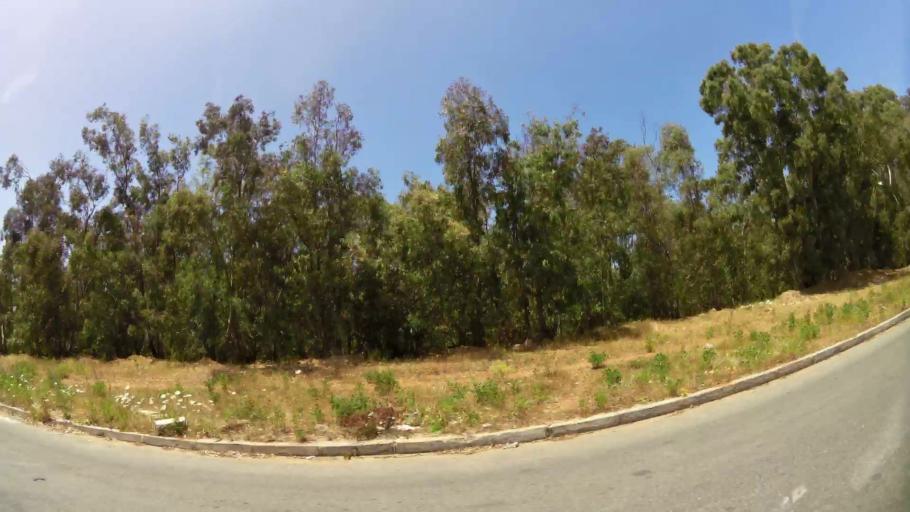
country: MA
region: Gharb-Chrarda-Beni Hssen
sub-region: Kenitra Province
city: Kenitra
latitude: 34.2699
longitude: -6.6327
